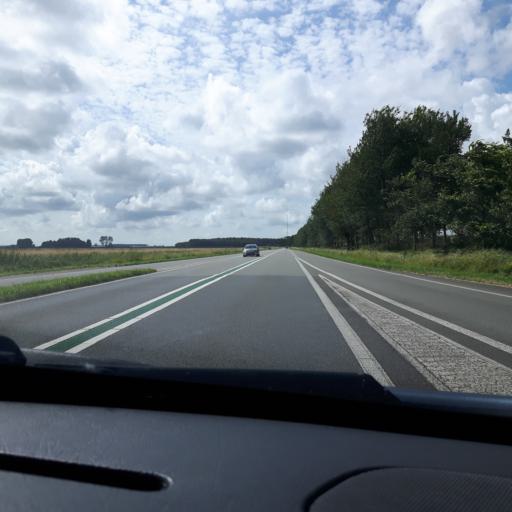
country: NL
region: Zeeland
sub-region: Gemeente Noord-Beveland
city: Kamperland
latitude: 51.5794
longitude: 3.8038
